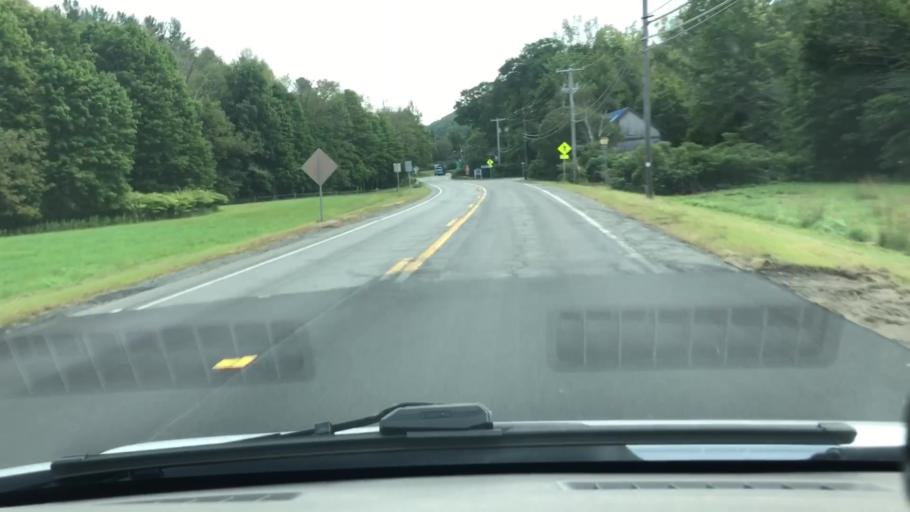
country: US
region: Massachusetts
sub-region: Franklin County
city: Charlemont
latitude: 42.6281
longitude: -72.8868
